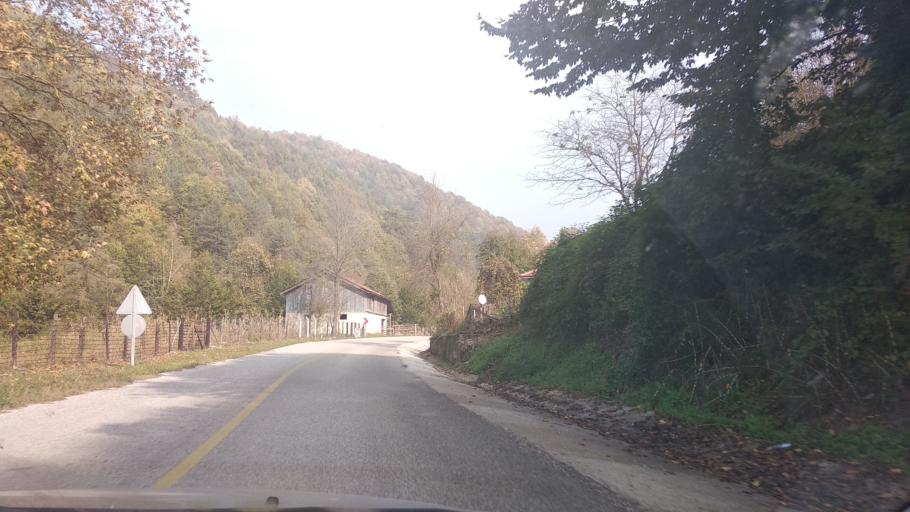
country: TR
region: Duzce
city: Kaynasli
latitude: 40.7270
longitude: 31.2489
